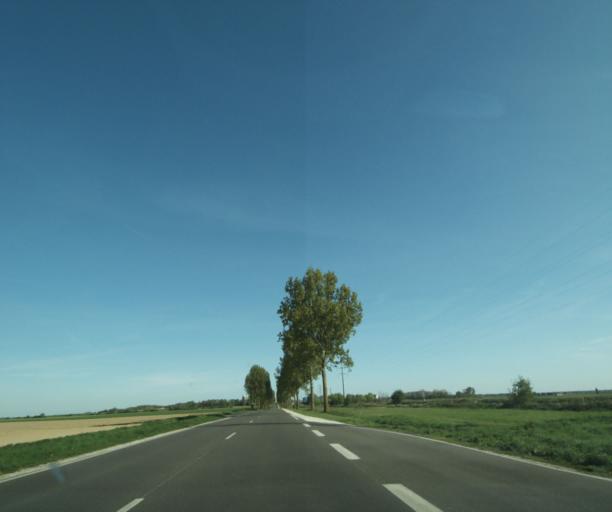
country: FR
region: Ile-de-France
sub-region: Departement de Seine-et-Marne
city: Bailly-Carrois
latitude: 48.5732
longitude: 2.9968
